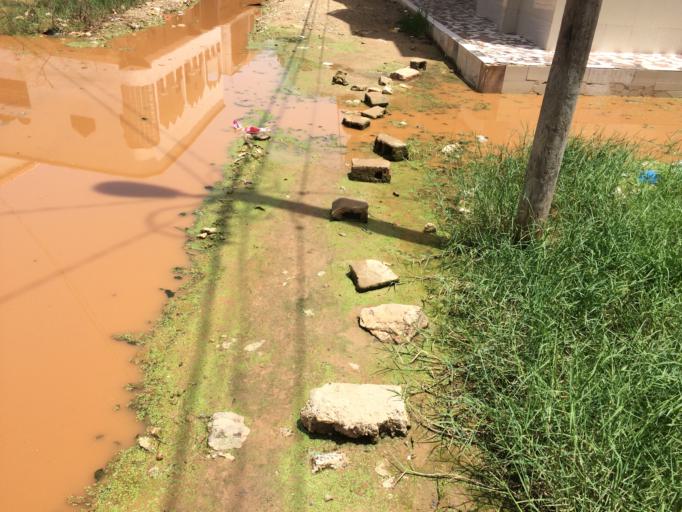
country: SN
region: Dakar
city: Pikine
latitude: 14.7377
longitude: -17.3312
